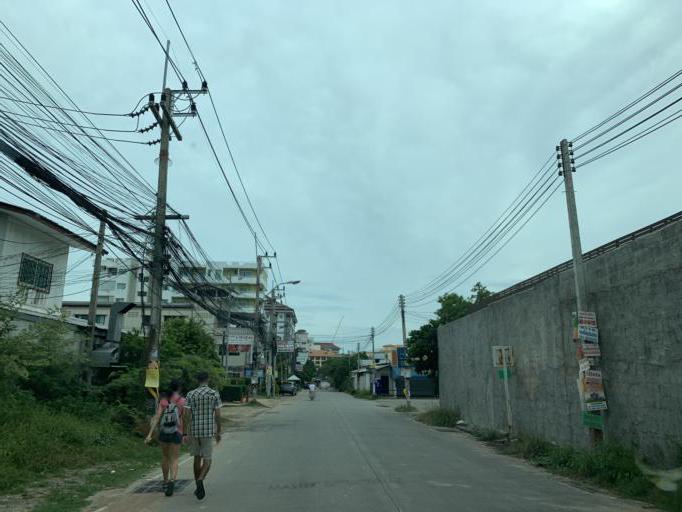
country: TH
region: Chon Buri
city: Phatthaya
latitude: 12.8984
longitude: 100.8764
